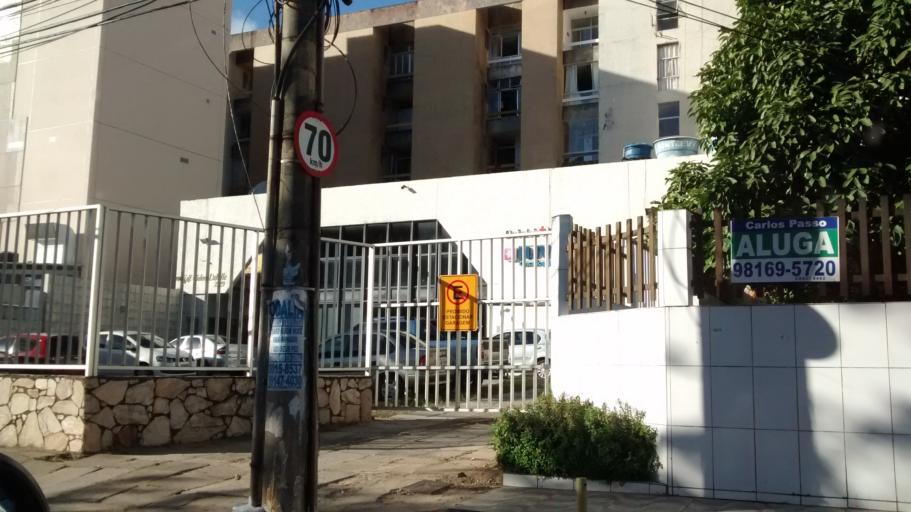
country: BR
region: Bahia
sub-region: Salvador
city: Salvador
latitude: -13.0066
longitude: -38.4997
